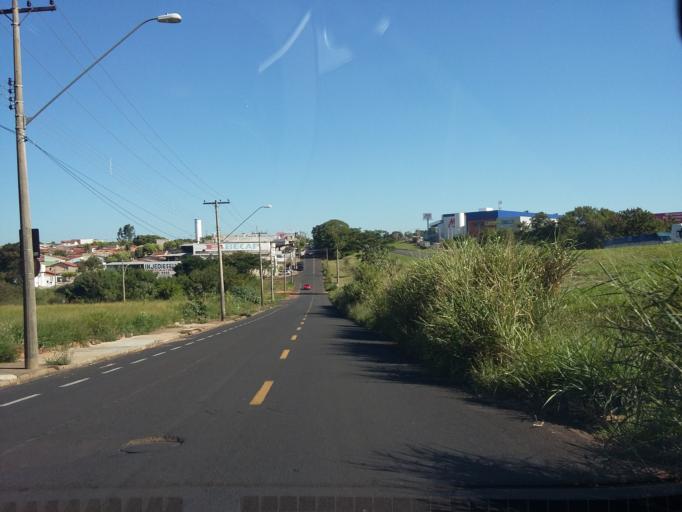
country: BR
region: Sao Paulo
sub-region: Sao Jose Do Rio Preto
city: Sao Jose do Rio Preto
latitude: -20.8370
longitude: -49.3664
